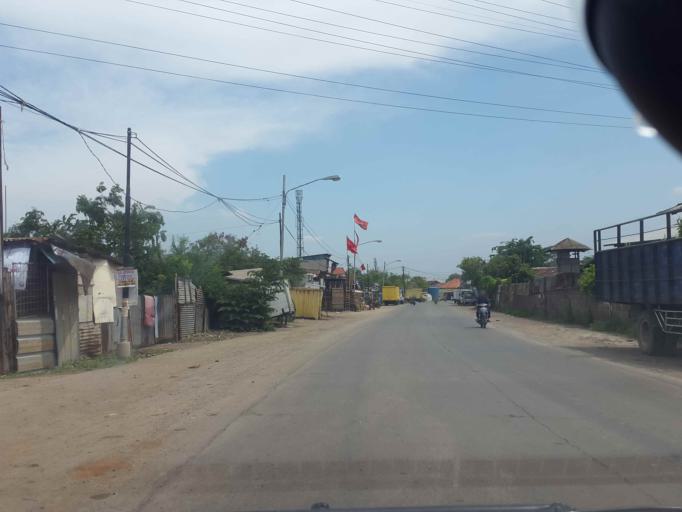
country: ID
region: Banten
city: Tangerang
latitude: -6.1536
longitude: 106.6589
